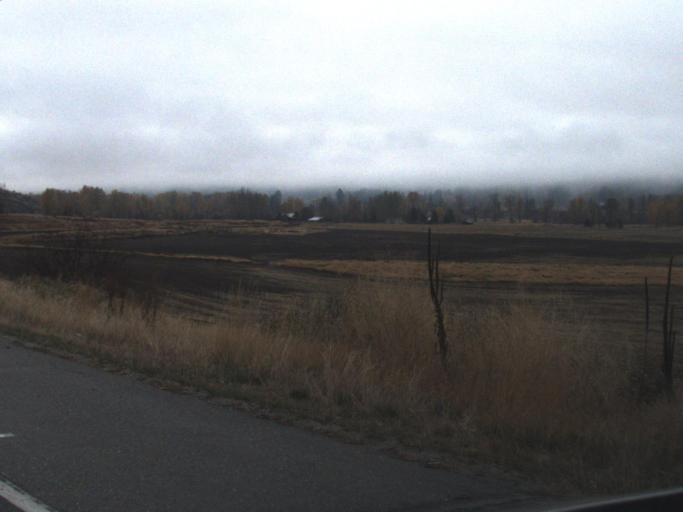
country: US
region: Washington
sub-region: Stevens County
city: Kettle Falls
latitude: 48.5978
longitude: -118.0088
